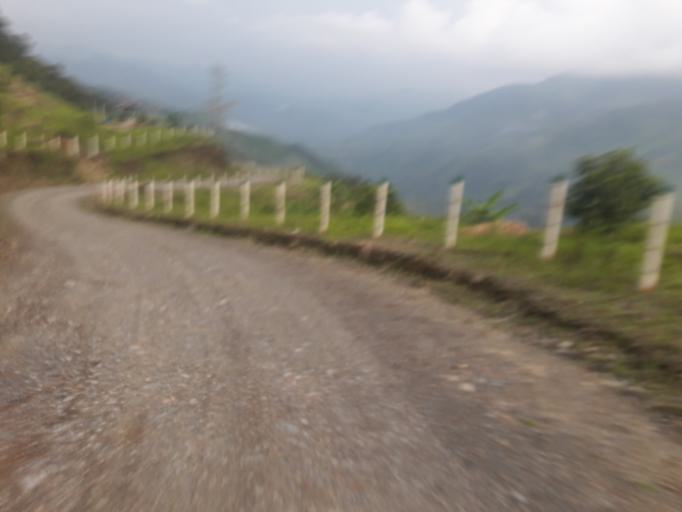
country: CO
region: Boyaca
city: Quipama
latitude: 5.5357
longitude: -74.1890
